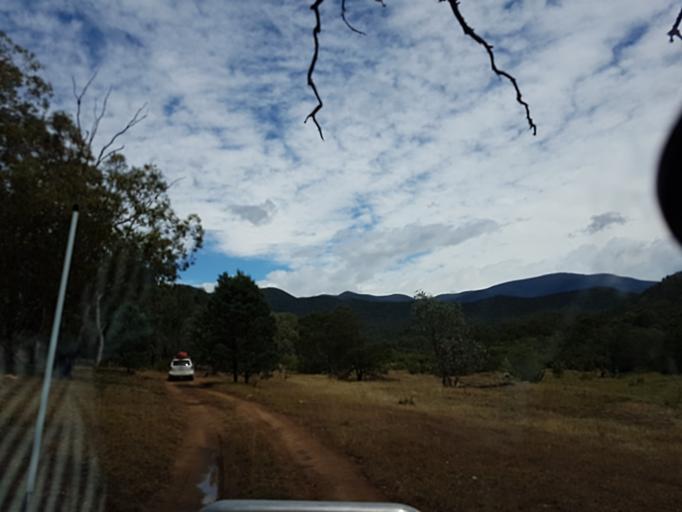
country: AU
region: New South Wales
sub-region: Snowy River
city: Jindabyne
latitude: -36.9511
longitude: 148.4017
